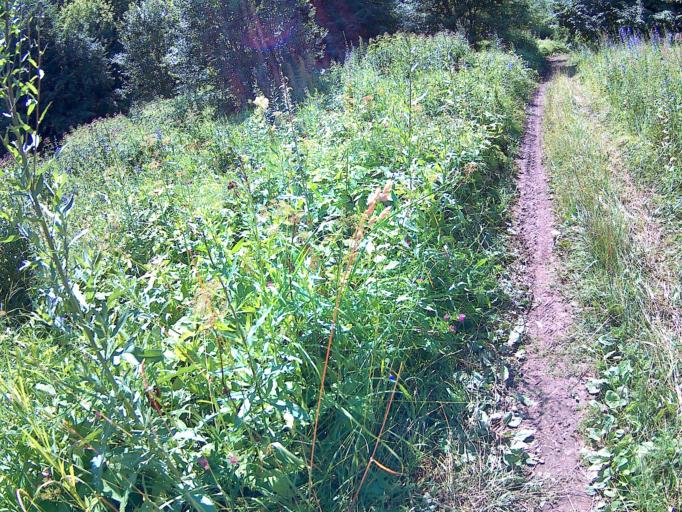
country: RU
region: Nizjnij Novgorod
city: Nizhniy Novgorod
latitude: 56.2421
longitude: 43.9413
